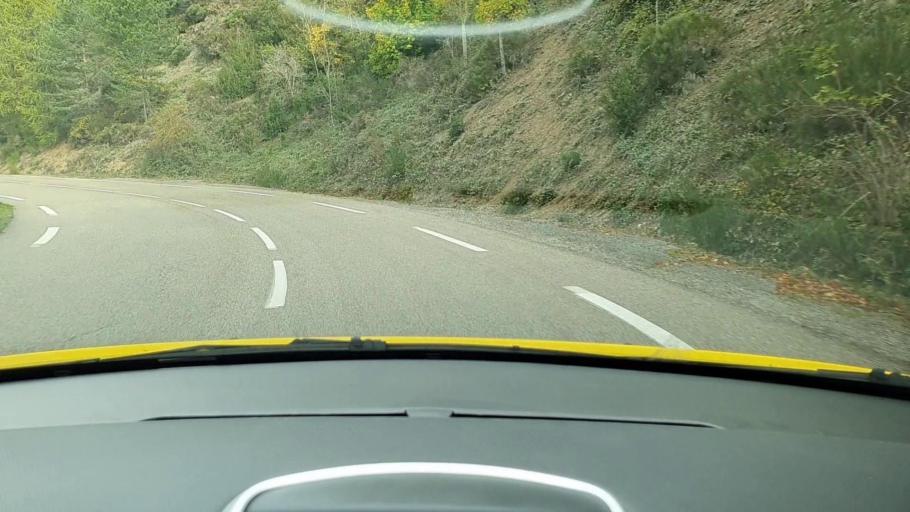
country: FR
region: Languedoc-Roussillon
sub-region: Departement de la Lozere
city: Meyrueis
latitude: 44.1239
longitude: 3.4486
